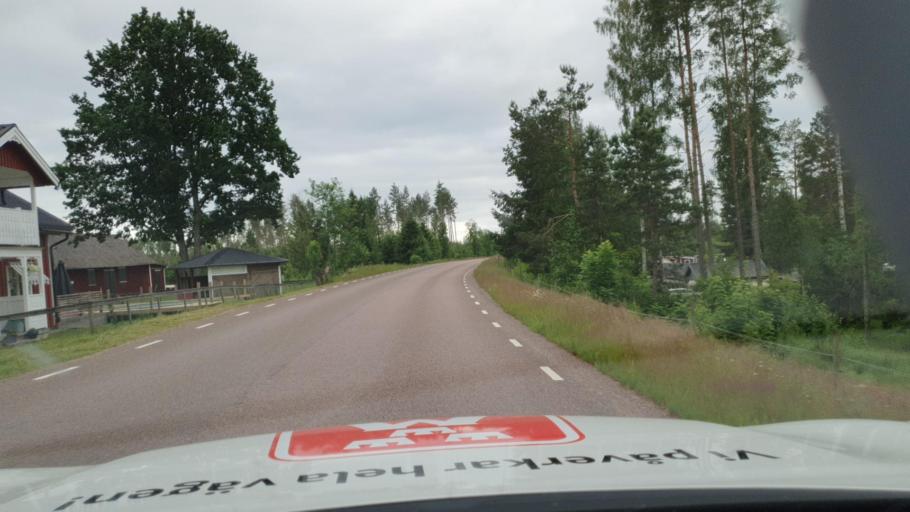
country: SE
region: Vaermland
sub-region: Forshaga Kommun
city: Forshaga
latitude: 59.4979
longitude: 13.4023
